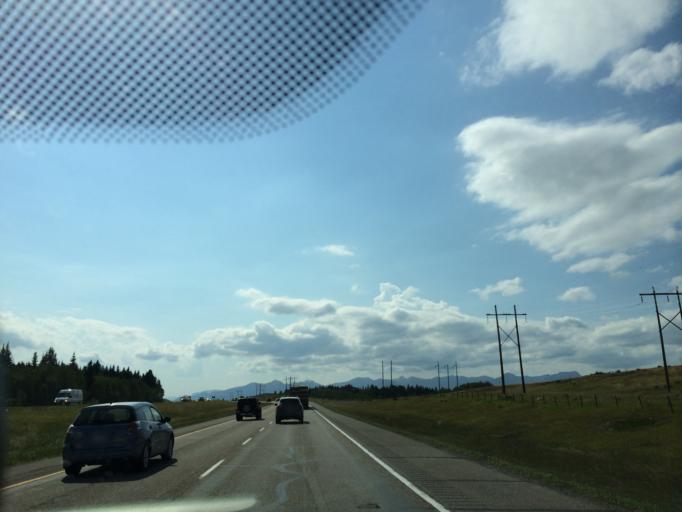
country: CA
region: Alberta
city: Cochrane
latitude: 51.1464
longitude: -114.8601
